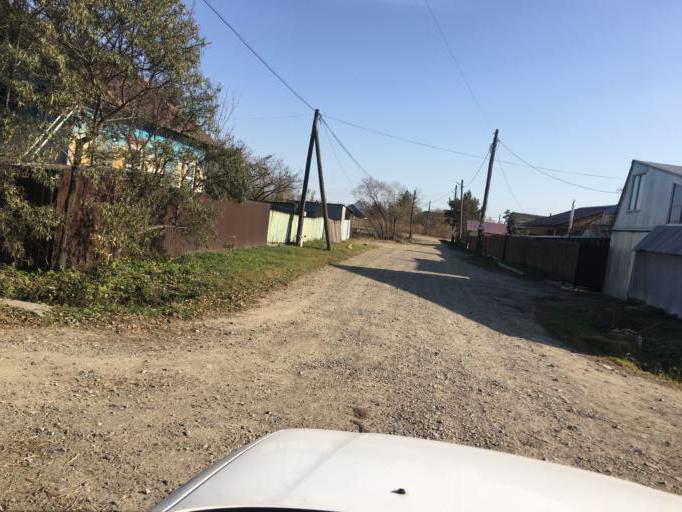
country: RU
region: Primorskiy
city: Dal'nerechensk
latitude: 45.9255
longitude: 133.7255
